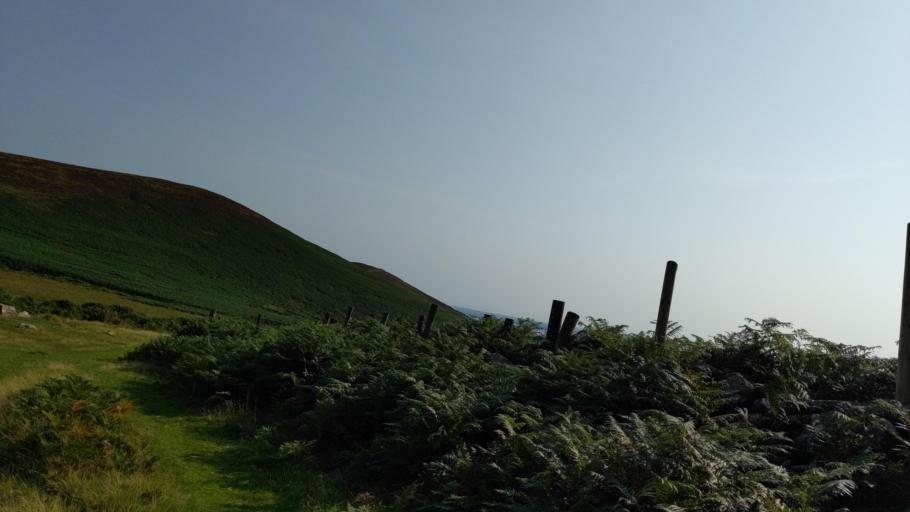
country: GB
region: Northern Ireland
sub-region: Down District
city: Warrenpoint
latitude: 54.0646
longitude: -6.3235
